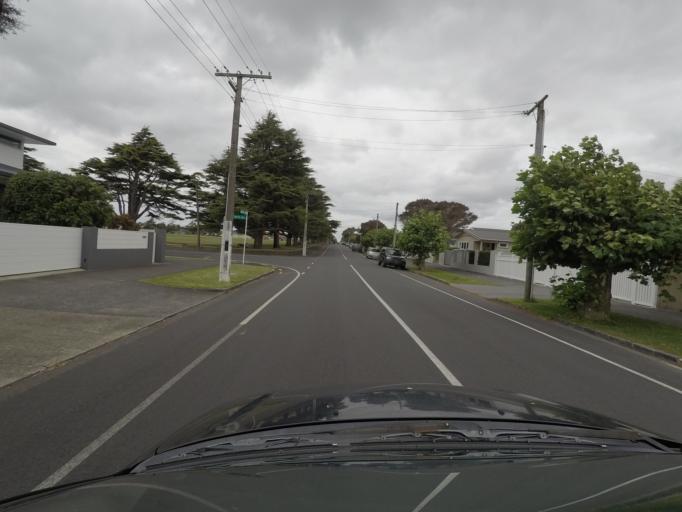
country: NZ
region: Auckland
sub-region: Auckland
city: Rosebank
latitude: -36.8665
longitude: 174.7025
